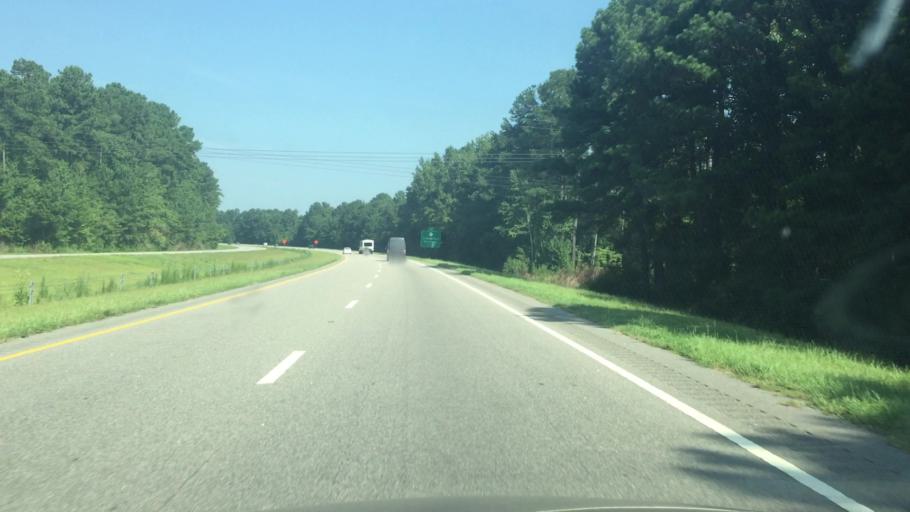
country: US
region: North Carolina
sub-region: Robeson County
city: Lumberton
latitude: 34.5667
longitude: -79.0290
